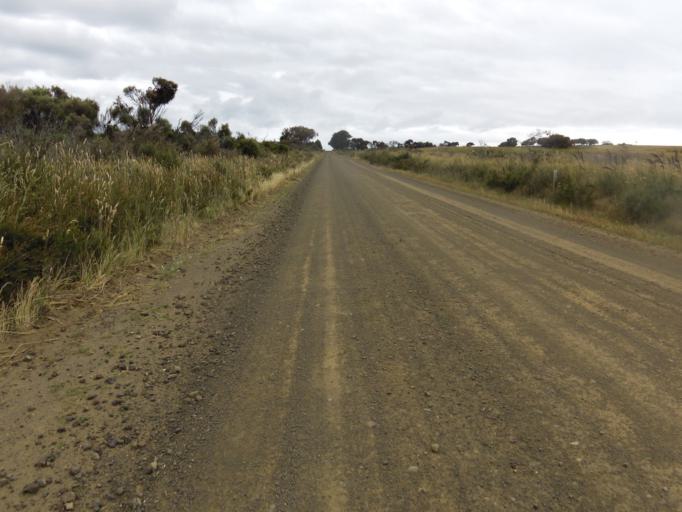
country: AU
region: Victoria
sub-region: Bass Coast
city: Cowes
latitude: -38.3803
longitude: 145.3534
